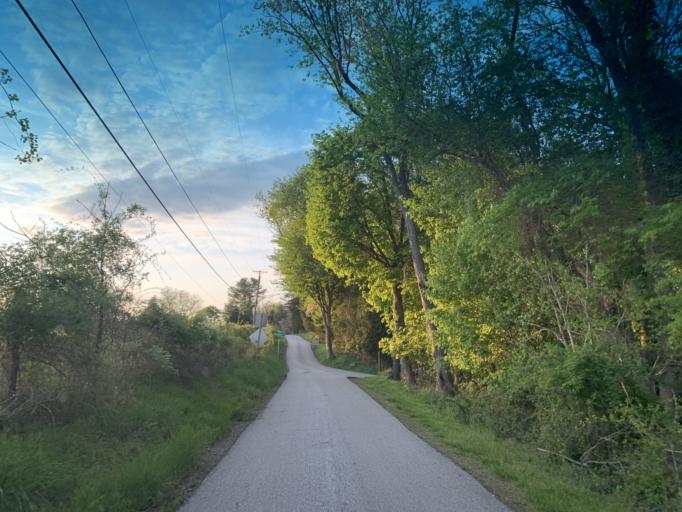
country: US
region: Maryland
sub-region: Harford County
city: Bel Air South
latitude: 39.4955
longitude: -76.3500
